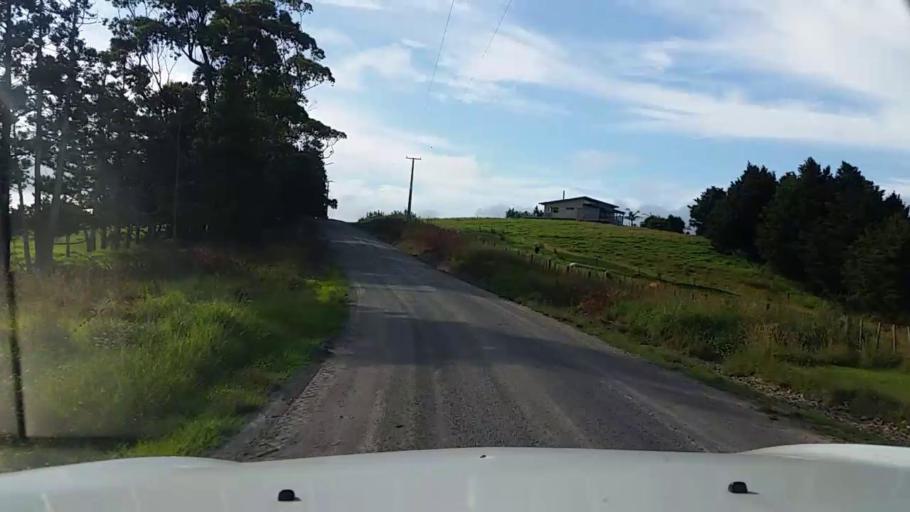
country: NZ
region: Northland
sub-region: Whangarei
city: Maungatapere
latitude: -35.6727
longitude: 174.1755
